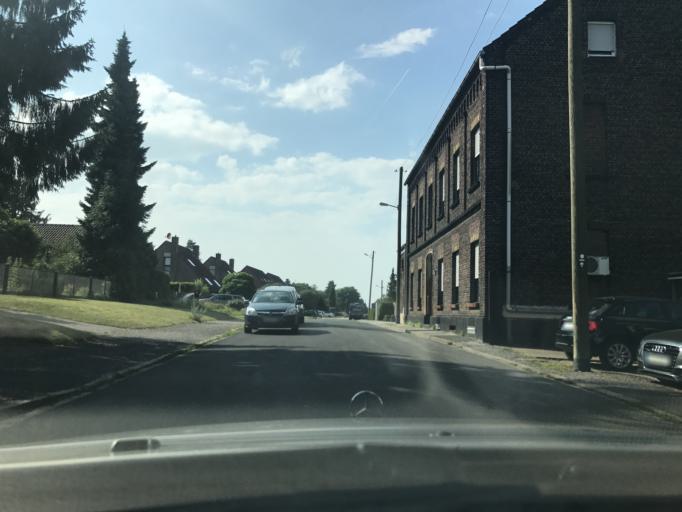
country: DE
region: North Rhine-Westphalia
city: Tonisvorst
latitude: 51.3574
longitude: 6.5308
